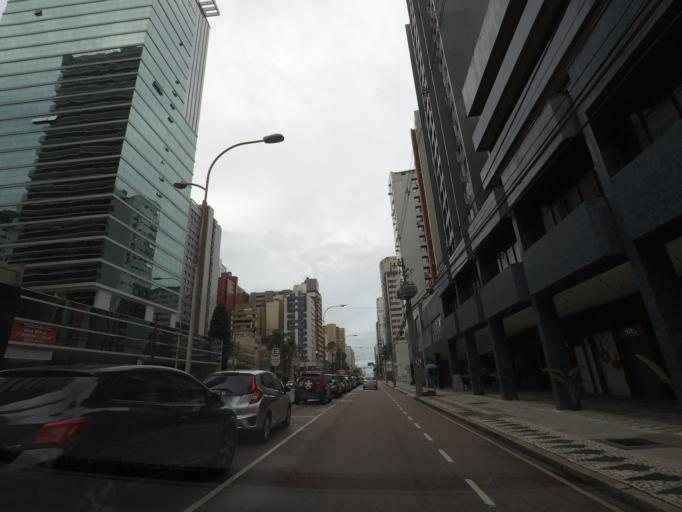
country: BR
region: Parana
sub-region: Curitiba
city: Curitiba
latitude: -25.4443
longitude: -49.2839
